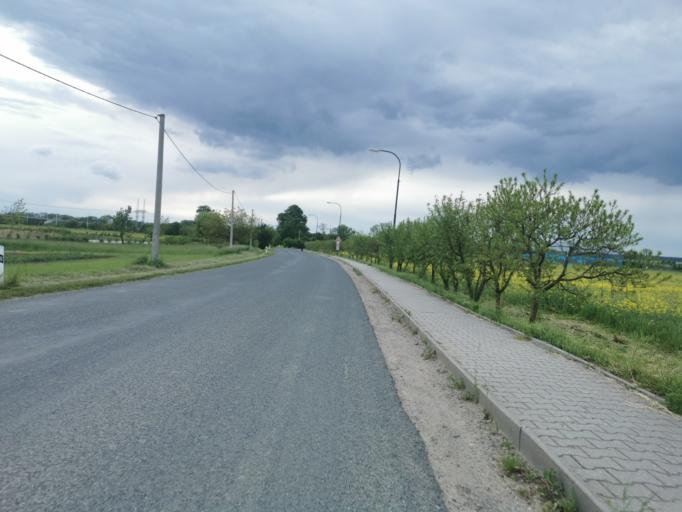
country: CZ
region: South Moravian
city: Sudomerice
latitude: 48.8715
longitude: 17.2477
